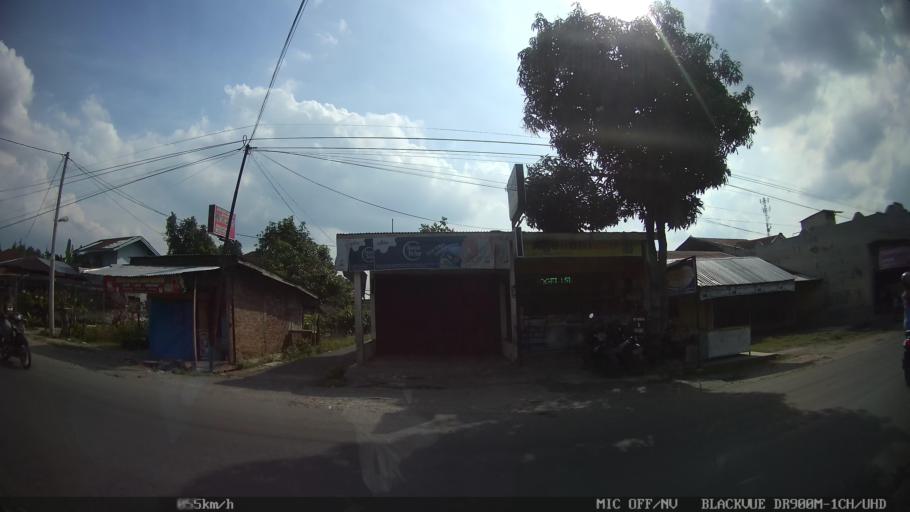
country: ID
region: North Sumatra
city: Binjai
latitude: 3.6314
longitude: 98.4911
